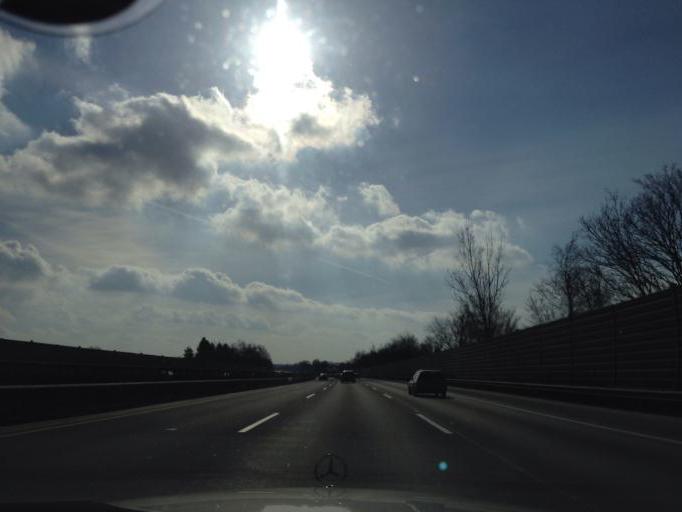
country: DE
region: Hamburg
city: Harburg
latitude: 53.4201
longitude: 10.0319
